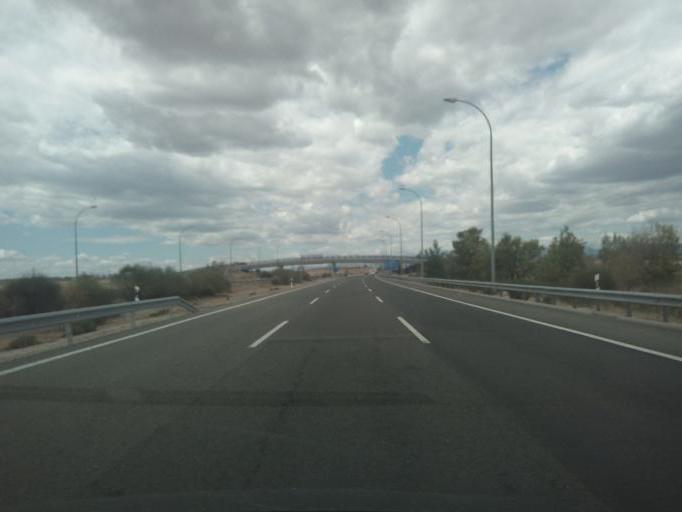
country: ES
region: Madrid
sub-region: Provincia de Madrid
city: San Sebastian de los Reyes
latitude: 40.5481
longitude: -3.5750
